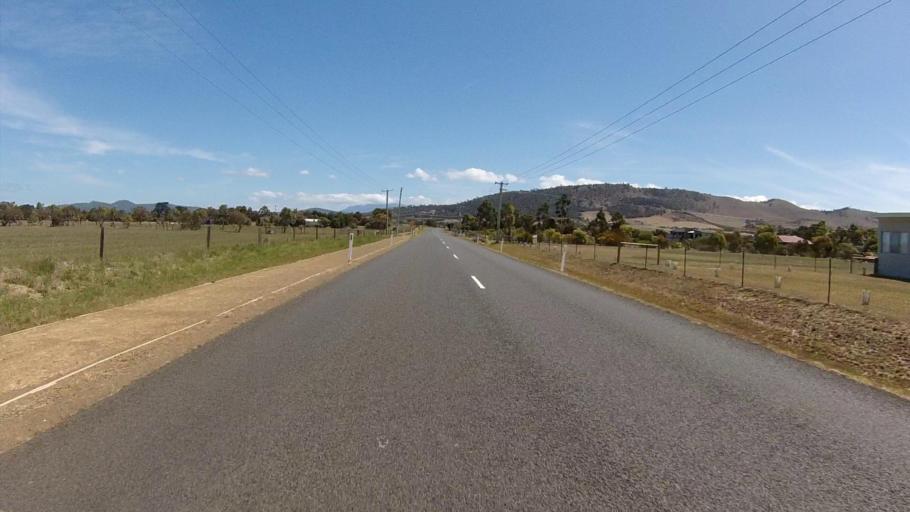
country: AU
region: Tasmania
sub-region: Sorell
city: Sorell
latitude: -42.7778
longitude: 147.5265
